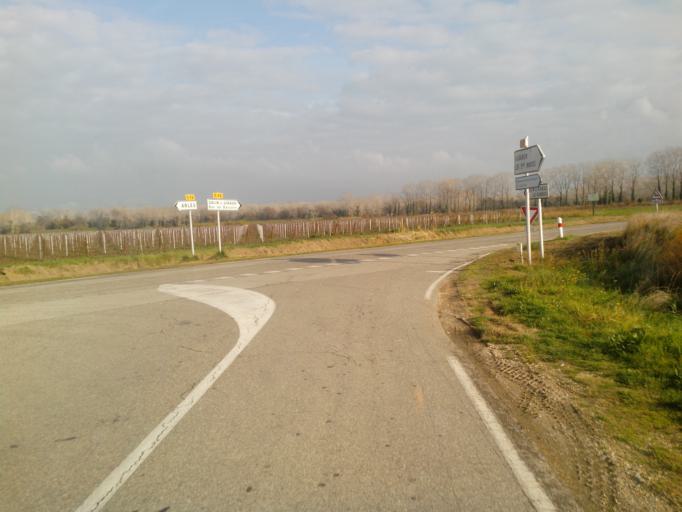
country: FR
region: Provence-Alpes-Cote d'Azur
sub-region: Departement des Bouches-du-Rhone
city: Arles
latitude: 43.5816
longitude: 4.6528
